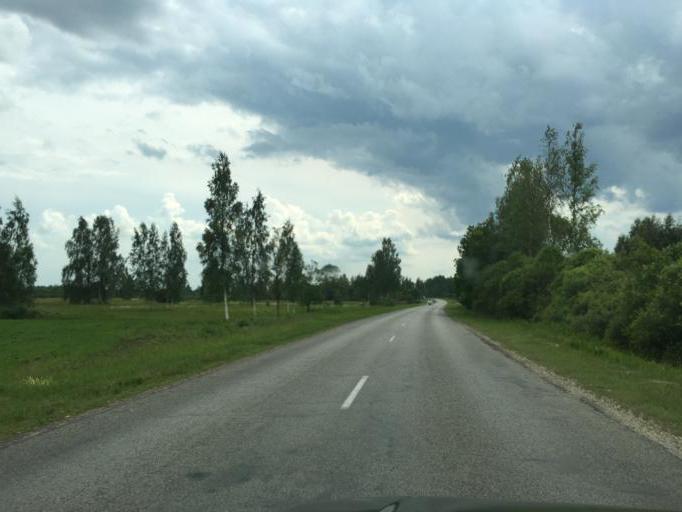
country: LV
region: Rugaju
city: Rugaji
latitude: 56.9418
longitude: 27.0681
